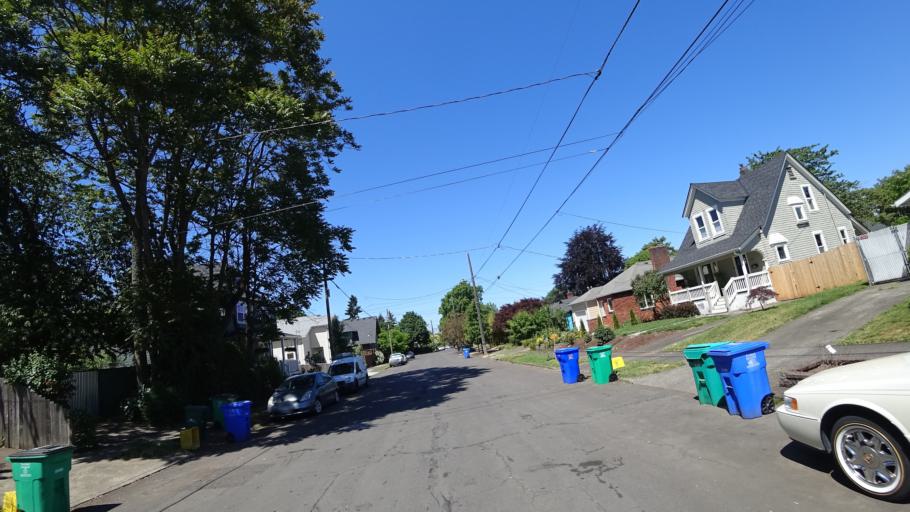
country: US
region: Oregon
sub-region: Multnomah County
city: Portland
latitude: 45.5655
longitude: -122.6541
